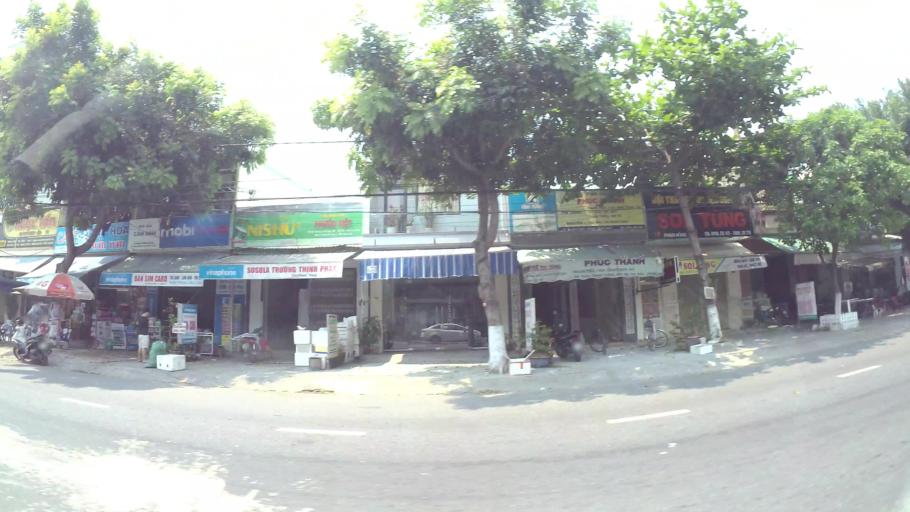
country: VN
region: Da Nang
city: Cam Le
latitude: 16.0016
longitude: 108.2070
